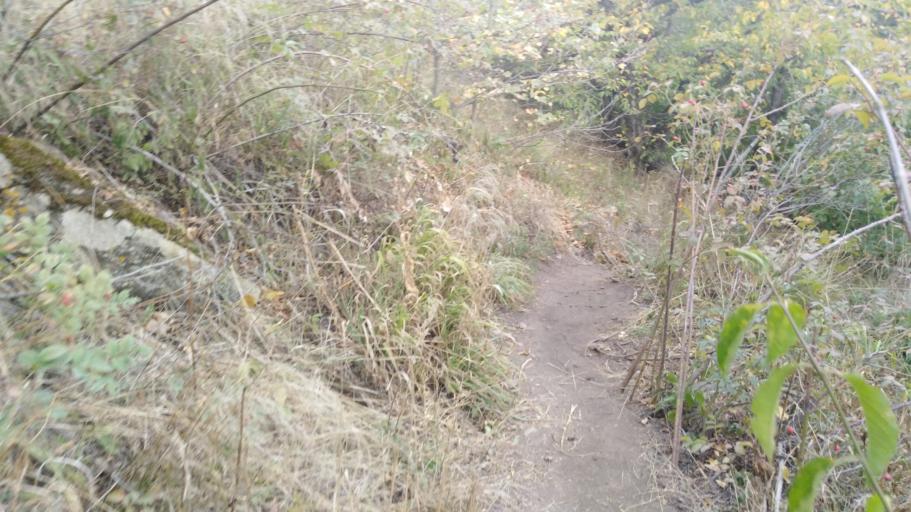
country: RU
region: Stavropol'skiy
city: Zheleznovodsk
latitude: 44.0962
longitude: 43.0276
